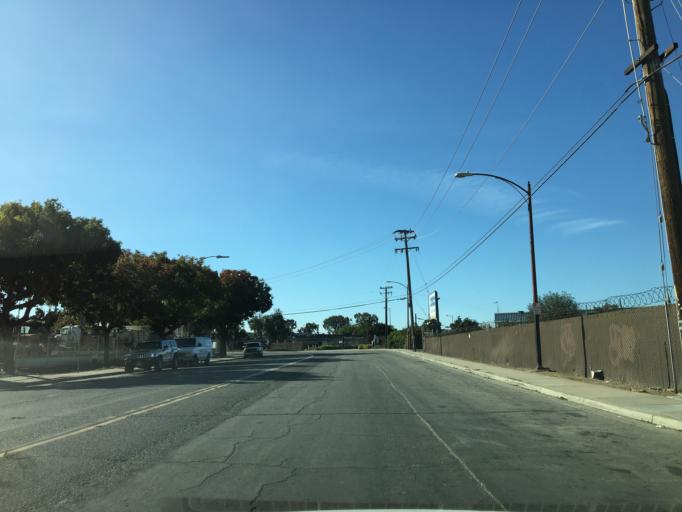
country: US
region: California
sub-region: Santa Clara County
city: San Jose
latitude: 37.3629
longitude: -121.8759
